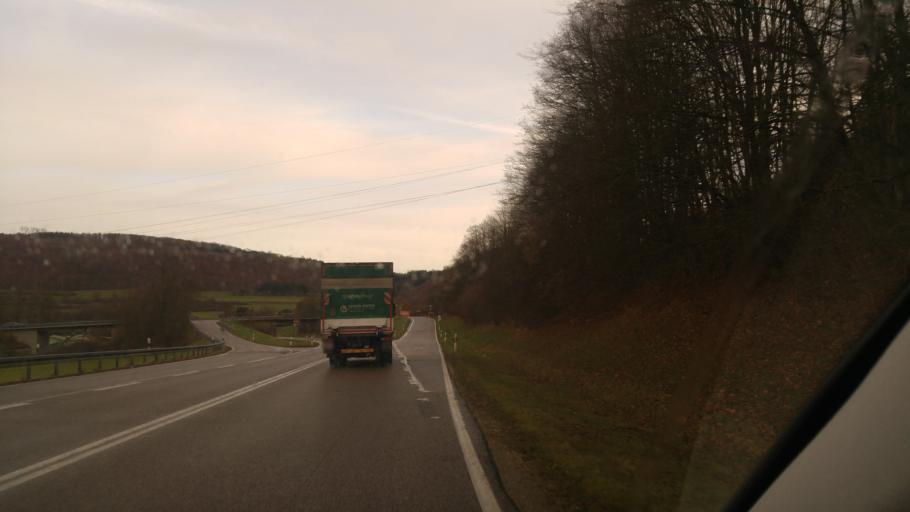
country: DE
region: Baden-Wuerttemberg
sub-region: Regierungsbezirk Stuttgart
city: Oberkochen
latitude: 48.7836
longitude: 10.1158
